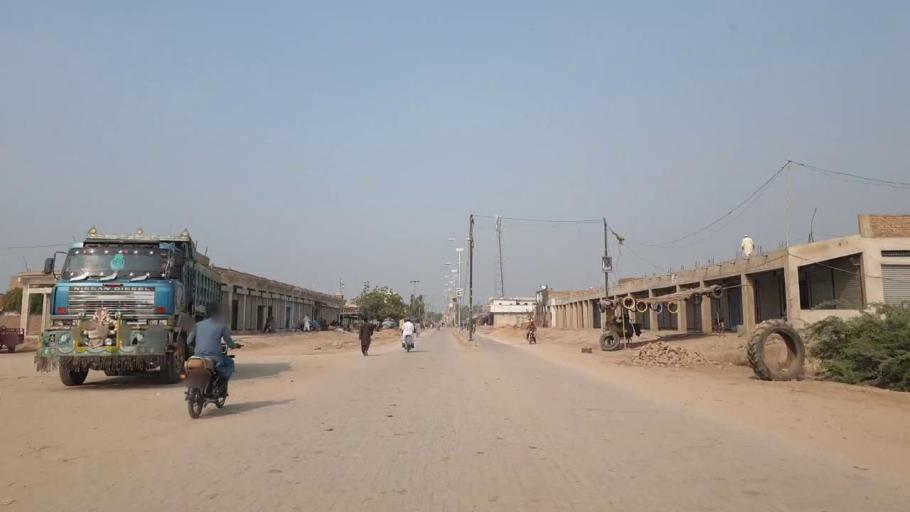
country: PK
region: Sindh
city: Bhan
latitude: 26.5491
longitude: 67.7183
